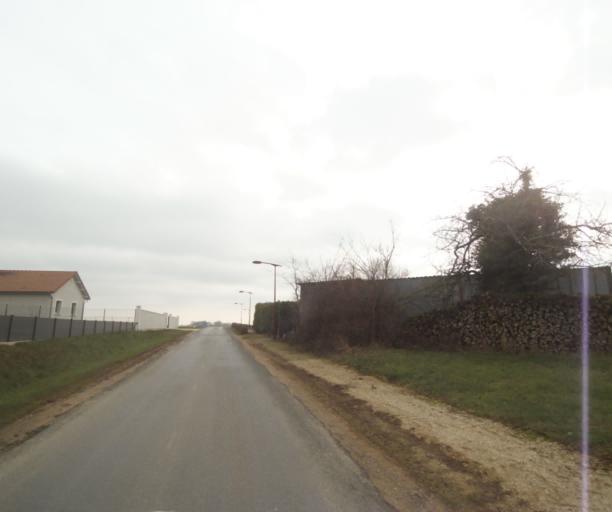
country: FR
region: Champagne-Ardenne
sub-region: Departement de la Marne
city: Pargny-sur-Saulx
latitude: 48.6913
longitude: 4.8055
